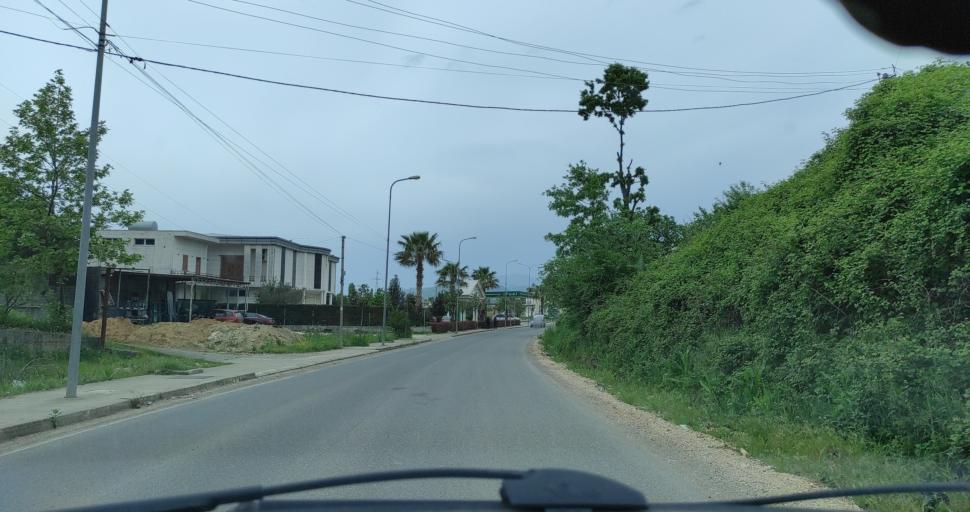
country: AL
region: Lezhe
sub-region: Rrethi i Kurbinit
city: Lac
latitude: 41.6234
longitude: 19.7085
